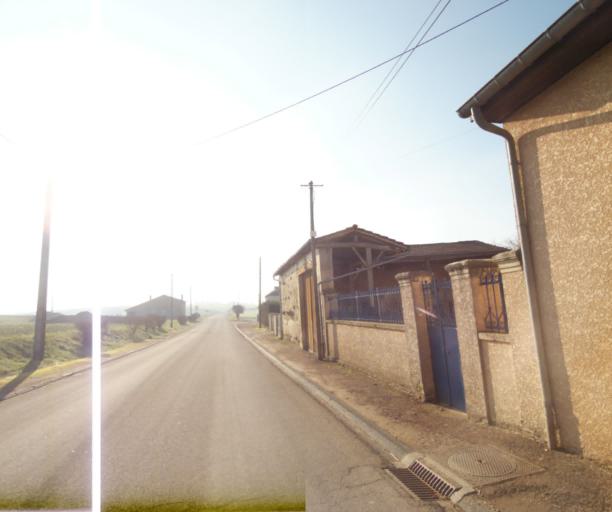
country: FR
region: Champagne-Ardenne
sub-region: Departement de la Haute-Marne
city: Wassy
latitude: 48.4540
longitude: 4.9622
